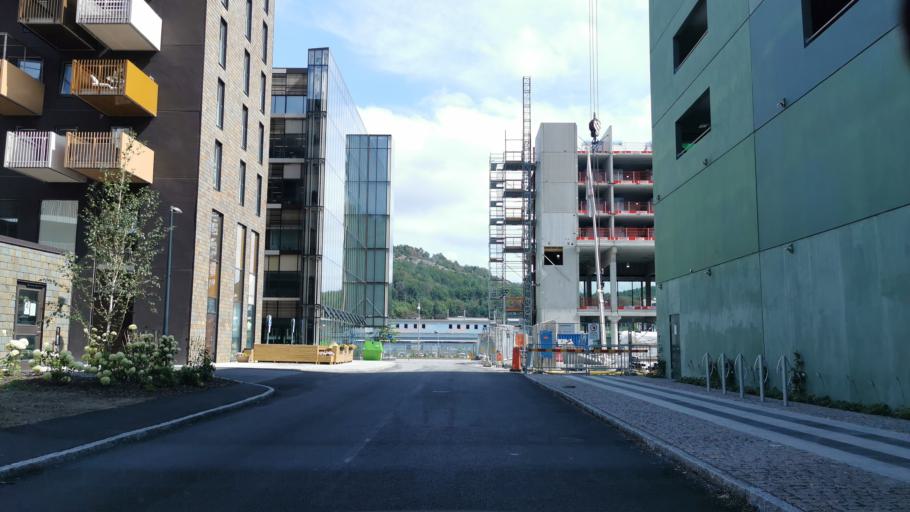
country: SE
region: Vaestra Goetaland
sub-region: Molndal
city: Moelndal
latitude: 57.6683
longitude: 12.0092
